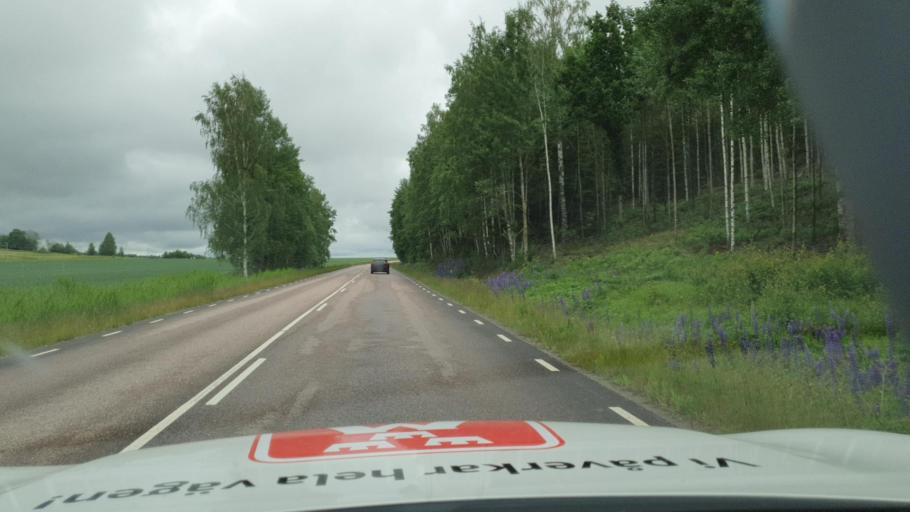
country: SE
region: Vaermland
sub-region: Karlstads Kommun
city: Edsvalla
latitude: 59.4057
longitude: 13.2103
